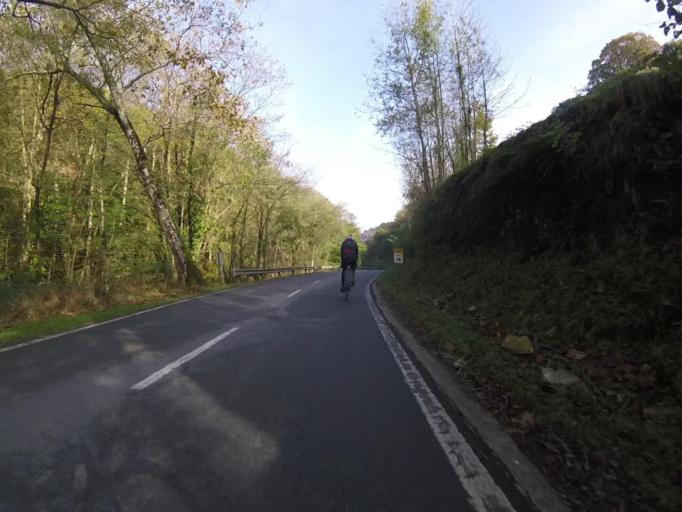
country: ES
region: Navarre
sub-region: Provincia de Navarra
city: Goizueta
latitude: 43.1811
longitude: -1.8610
